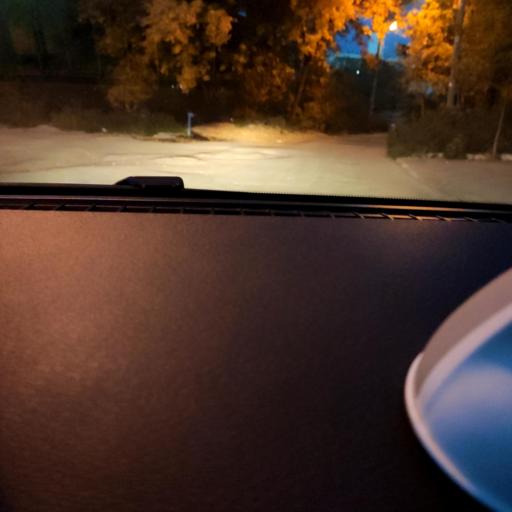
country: RU
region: Samara
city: Samara
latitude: 53.1876
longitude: 50.1508
